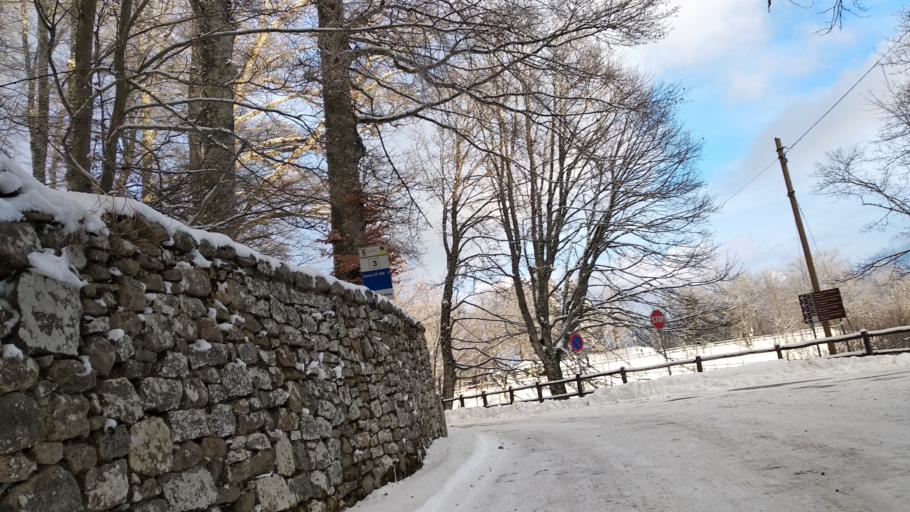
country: IT
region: Tuscany
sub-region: Province of Arezzo
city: Chiusi della Verna
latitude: 43.7076
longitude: 11.9359
